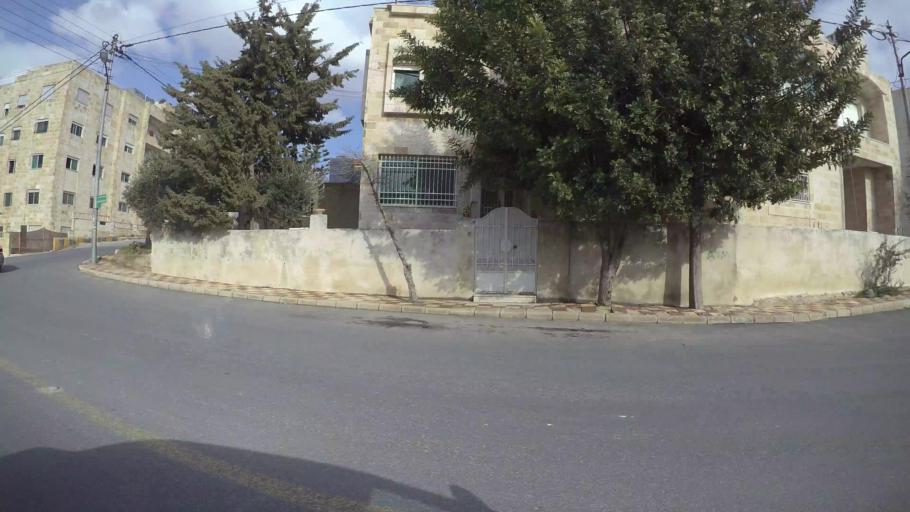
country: JO
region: Amman
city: Al Jubayhah
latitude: 32.0196
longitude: 35.8540
